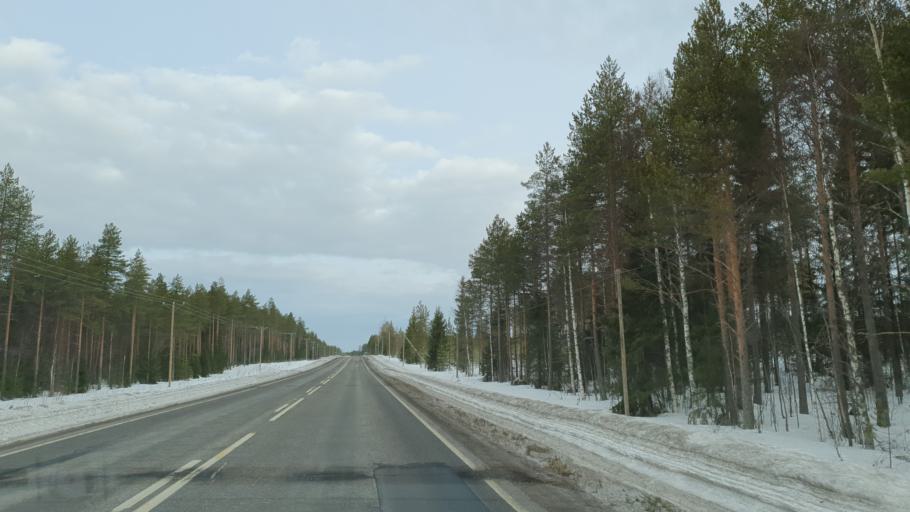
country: FI
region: Kainuu
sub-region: Kajaani
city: Vuokatti
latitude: 64.2098
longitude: 28.1415
